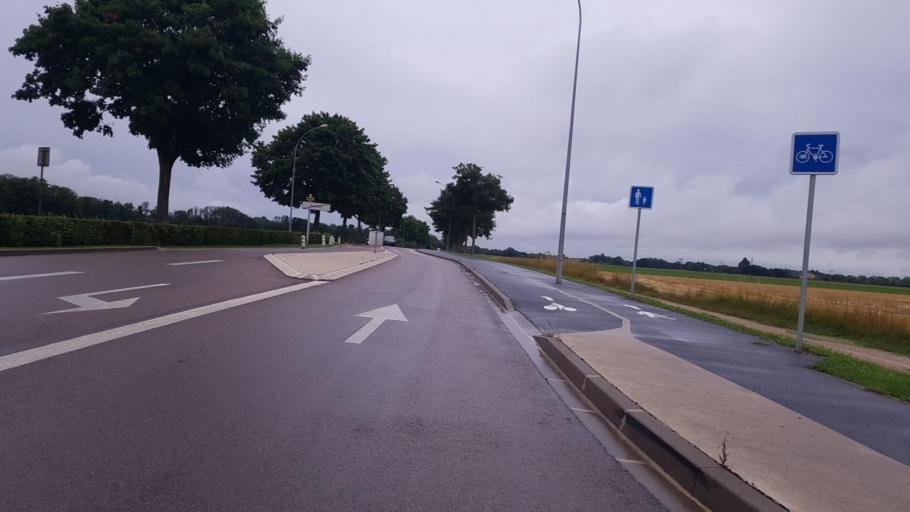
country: FR
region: Champagne-Ardenne
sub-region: Departement de la Marne
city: Sarry
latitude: 48.9232
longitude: 4.3998
